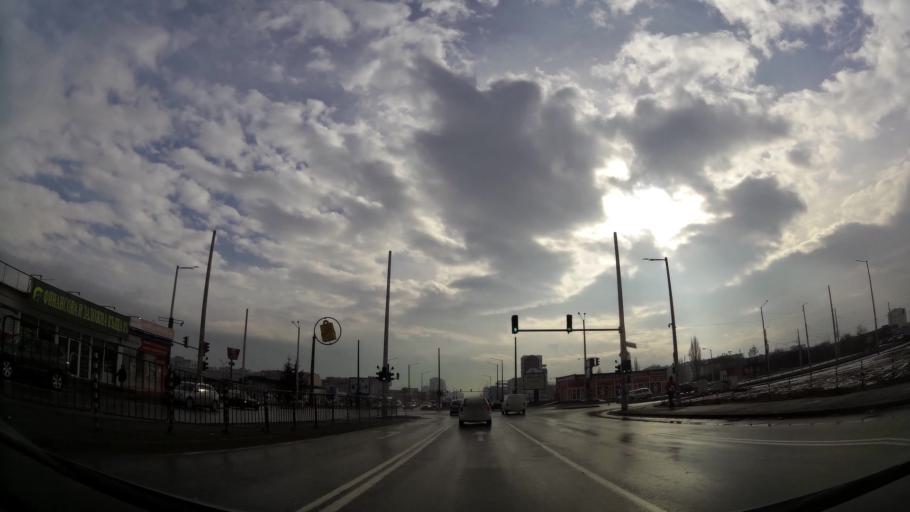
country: BG
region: Sofiya
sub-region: Obshtina Bozhurishte
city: Bozhurishte
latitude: 42.7199
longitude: 23.2543
